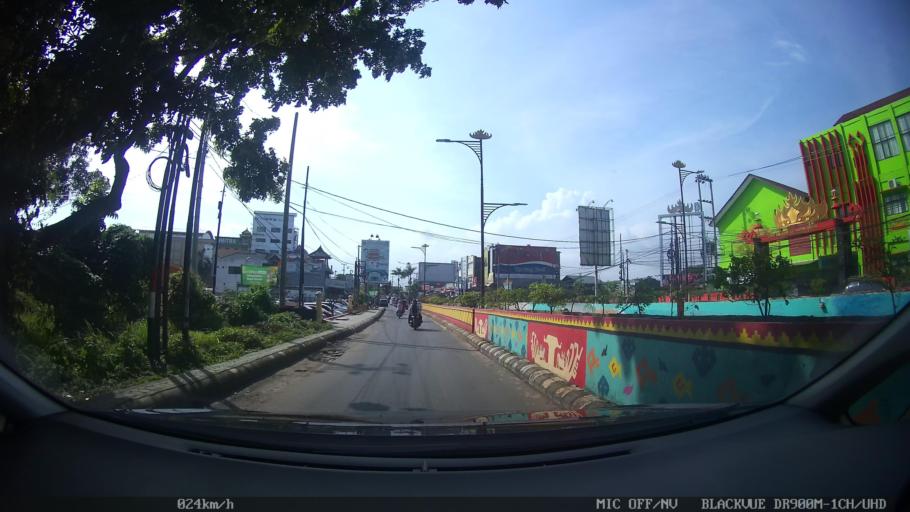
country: ID
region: Lampung
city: Kedaton
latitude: -5.3725
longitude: 105.2401
